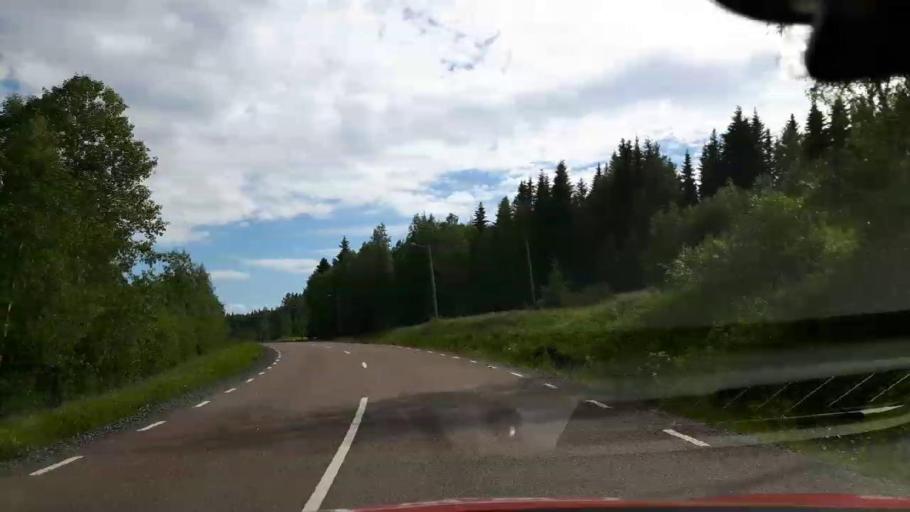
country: SE
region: Jaemtland
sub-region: Krokoms Kommun
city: Valla
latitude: 63.9325
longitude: 14.2108
